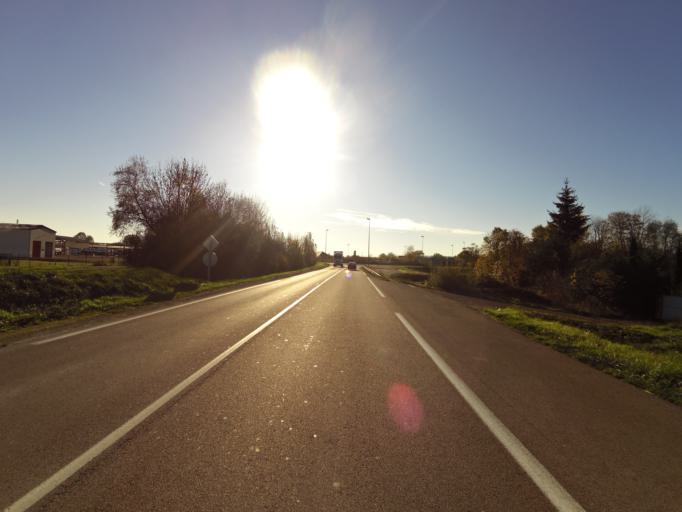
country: FR
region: Champagne-Ardenne
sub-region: Departement de l'Aube
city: Bucheres
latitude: 48.2280
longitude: 4.1303
